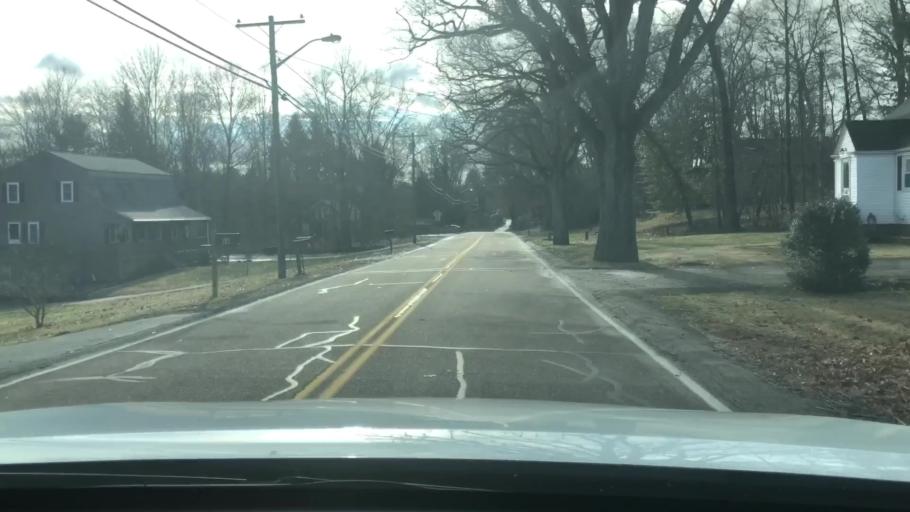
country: US
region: Massachusetts
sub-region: Worcester County
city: Blackstone
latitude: 42.0249
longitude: -71.5251
